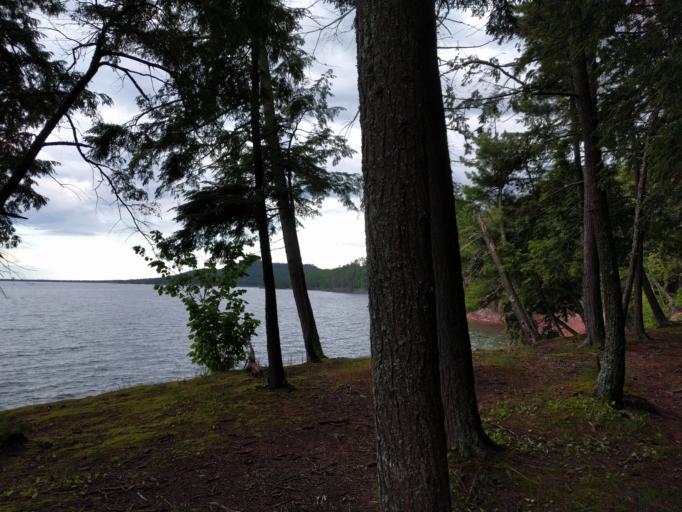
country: US
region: Michigan
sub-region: Marquette County
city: Trowbridge Park
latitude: 46.6275
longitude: -87.4678
